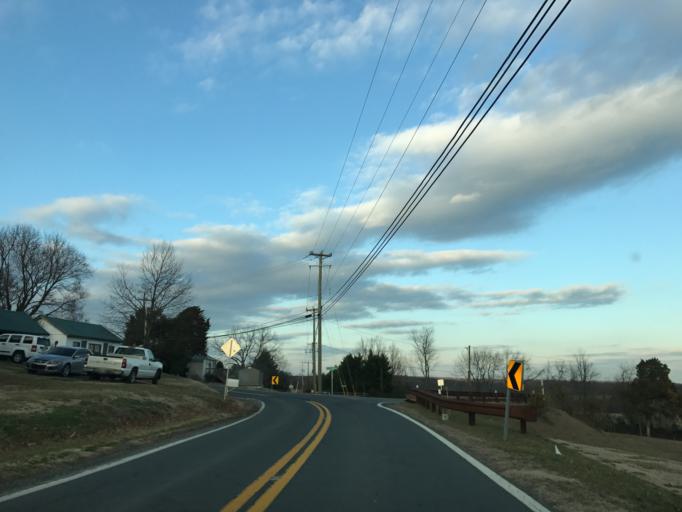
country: US
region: Maryland
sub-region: Cecil County
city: Charlestown
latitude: 39.5123
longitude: -75.9519
